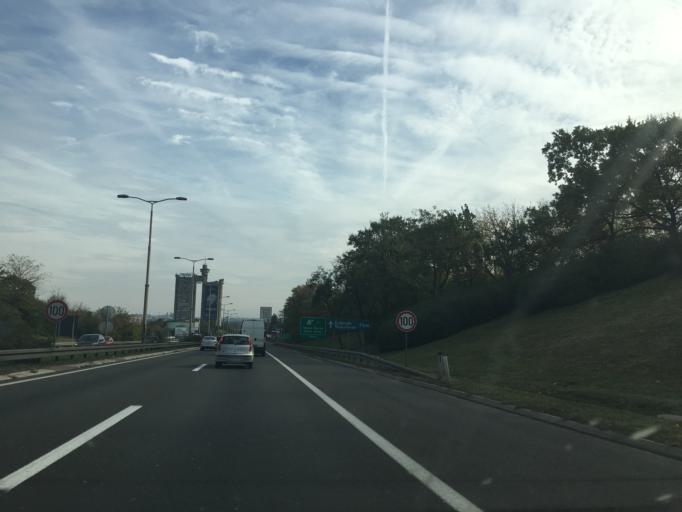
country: RS
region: Central Serbia
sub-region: Belgrade
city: Zemun
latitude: 44.8248
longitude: 20.3930
